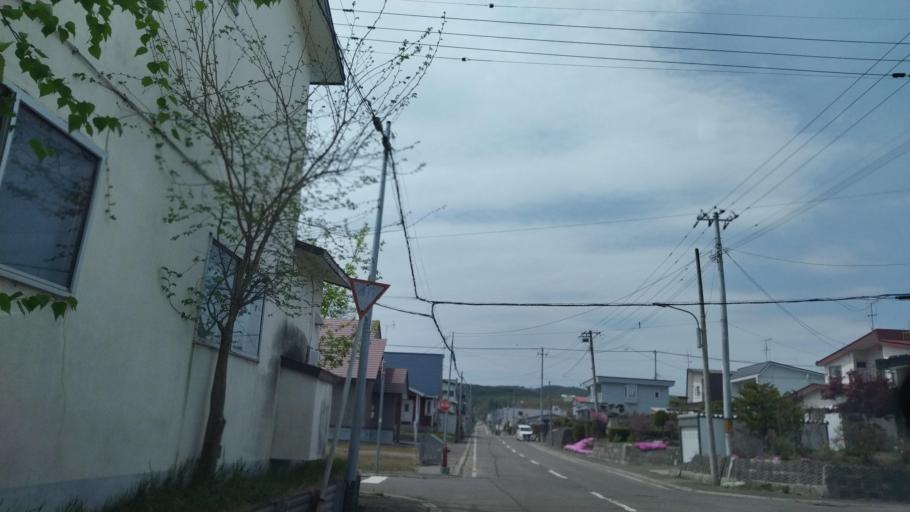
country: JP
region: Hokkaido
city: Otofuke
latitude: 43.2416
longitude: 143.5539
